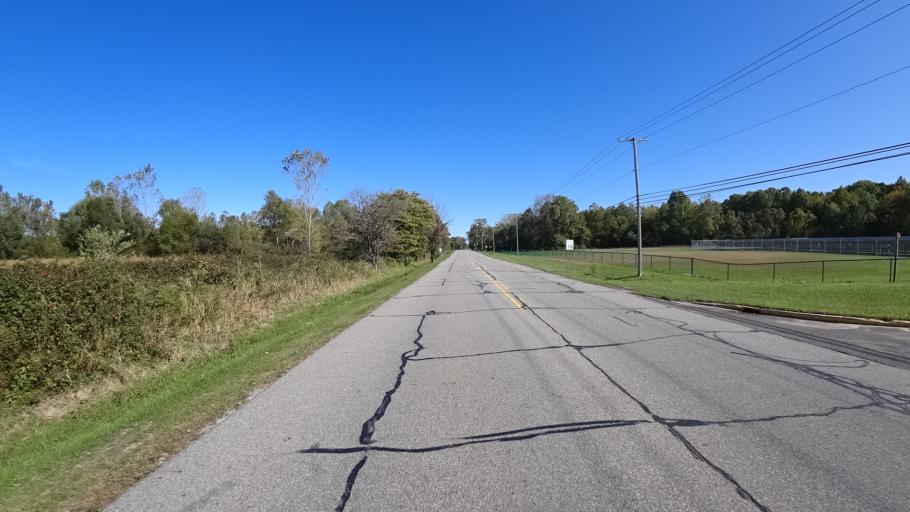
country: US
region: Indiana
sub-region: LaPorte County
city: Long Beach
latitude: 41.7239
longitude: -86.8386
